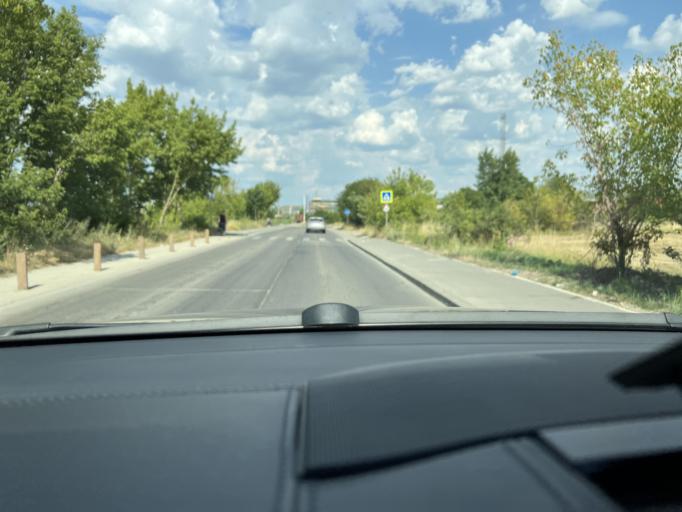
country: RO
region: Cluj
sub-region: Comuna Apahida
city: Dezmir
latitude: 46.7793
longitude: 23.6789
